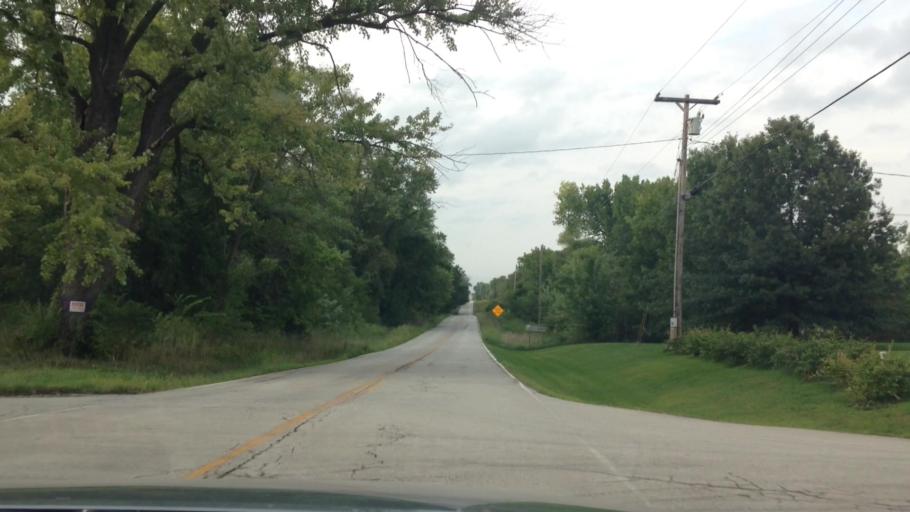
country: US
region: Missouri
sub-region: Clay County
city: Smithville
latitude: 39.3688
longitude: -94.6671
